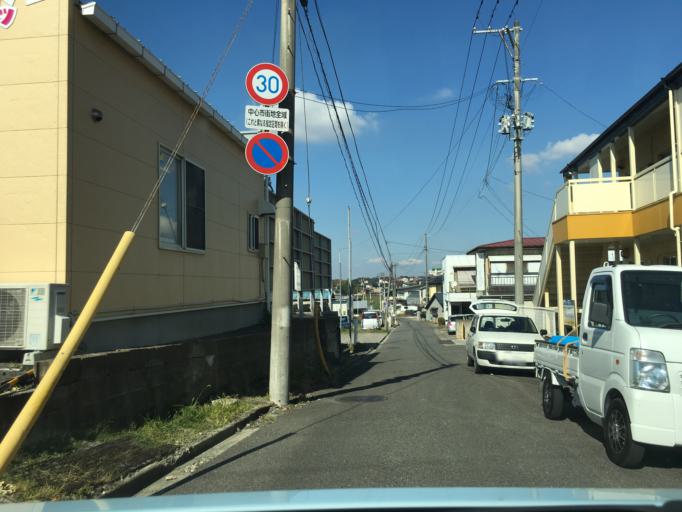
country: JP
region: Fukushima
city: Sukagawa
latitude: 37.2892
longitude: 140.3686
